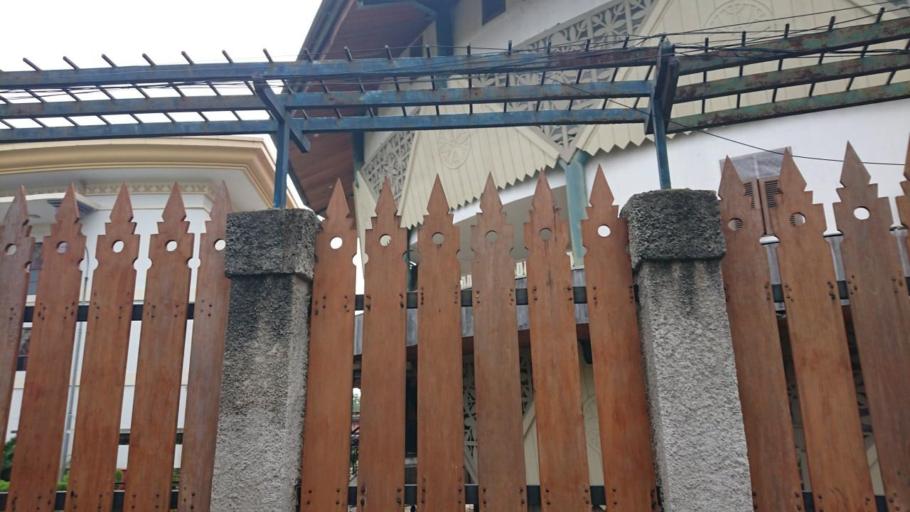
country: ID
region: West Java
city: Depok
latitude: -6.3389
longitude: 106.8251
